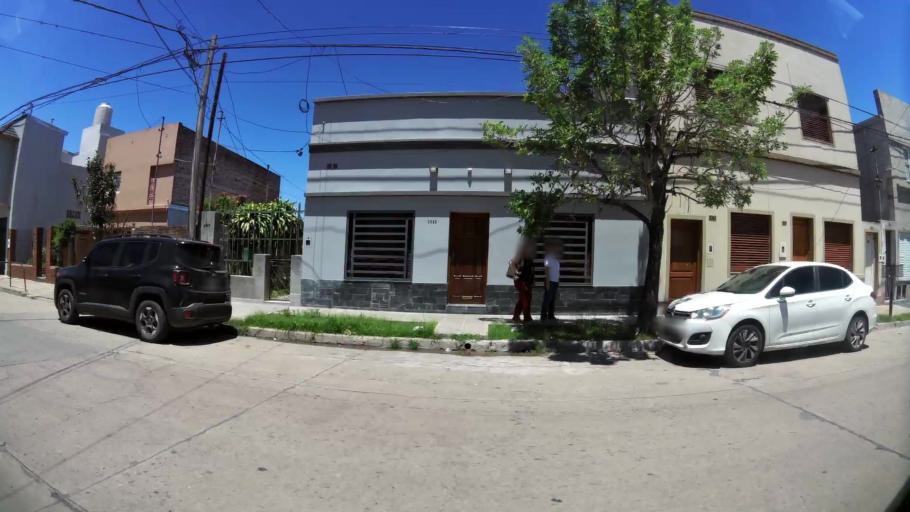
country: AR
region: Santa Fe
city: Santa Fe de la Vera Cruz
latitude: -31.6517
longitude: -60.7212
